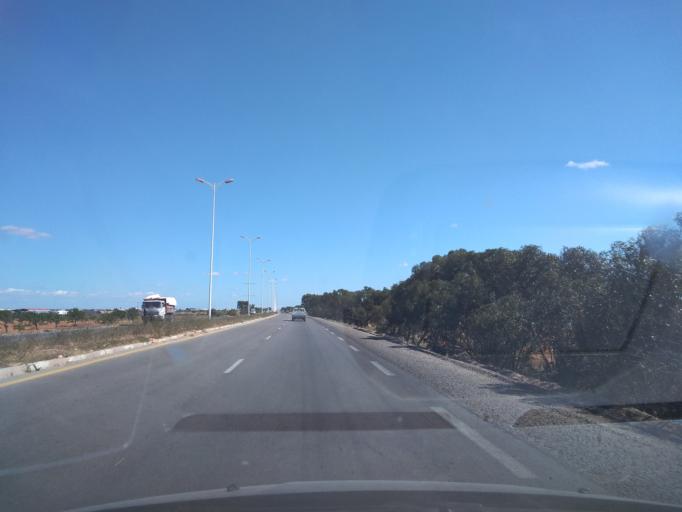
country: TN
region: Safaqis
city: Al Qarmadah
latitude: 34.8468
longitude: 10.7472
